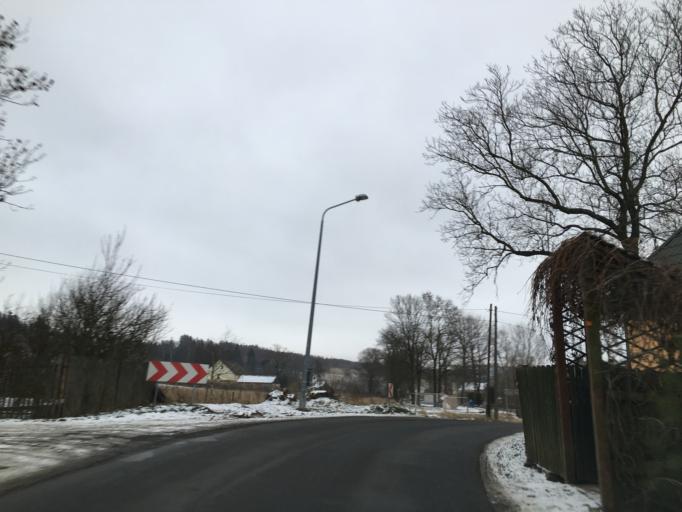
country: PL
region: Lower Silesian Voivodeship
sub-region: Powiat kamiennogorski
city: Krzeszow
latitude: 50.7042
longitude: 16.1177
